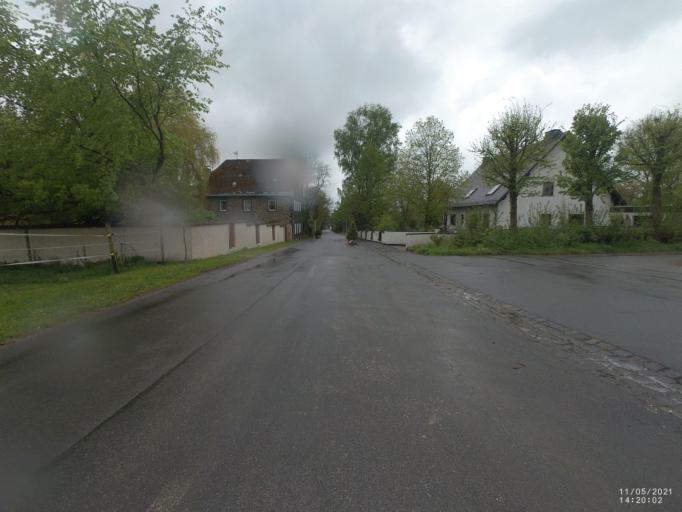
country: DE
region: Rheinland-Pfalz
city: Lonnig
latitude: 50.3300
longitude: 7.4195
